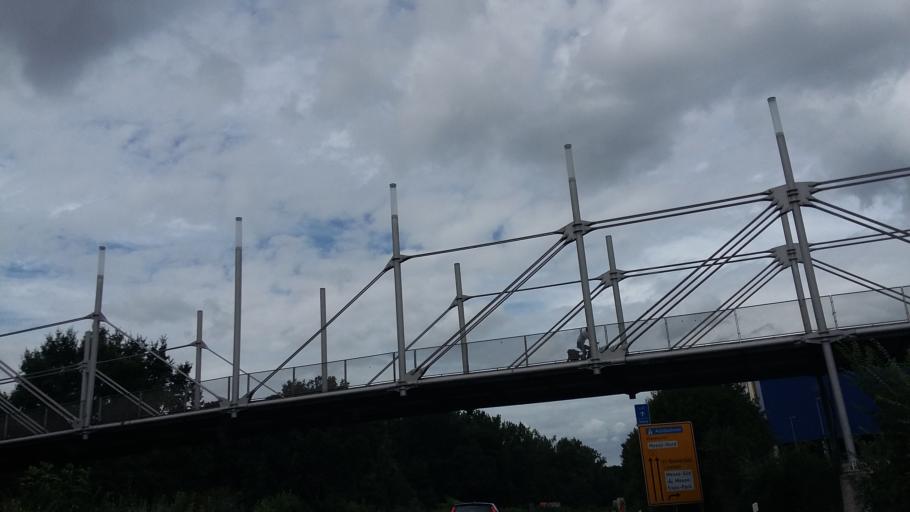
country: DE
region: Lower Saxony
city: Laatzen
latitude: 52.3118
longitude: 9.8171
